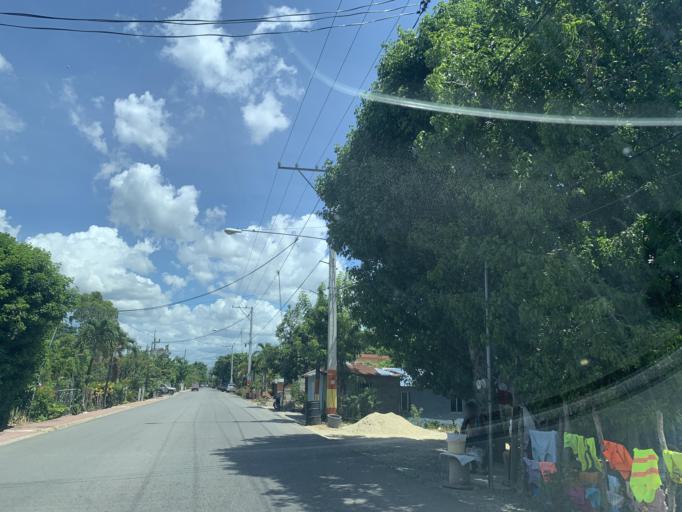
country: DO
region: Puerto Plata
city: Cabarete
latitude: 19.7031
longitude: -70.3834
